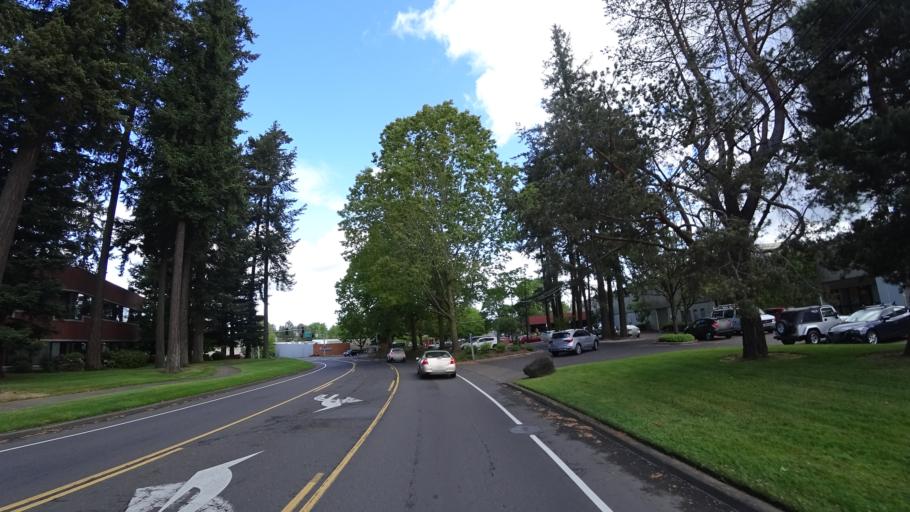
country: US
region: Oregon
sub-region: Washington County
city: Durham
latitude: 45.4031
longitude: -122.7491
